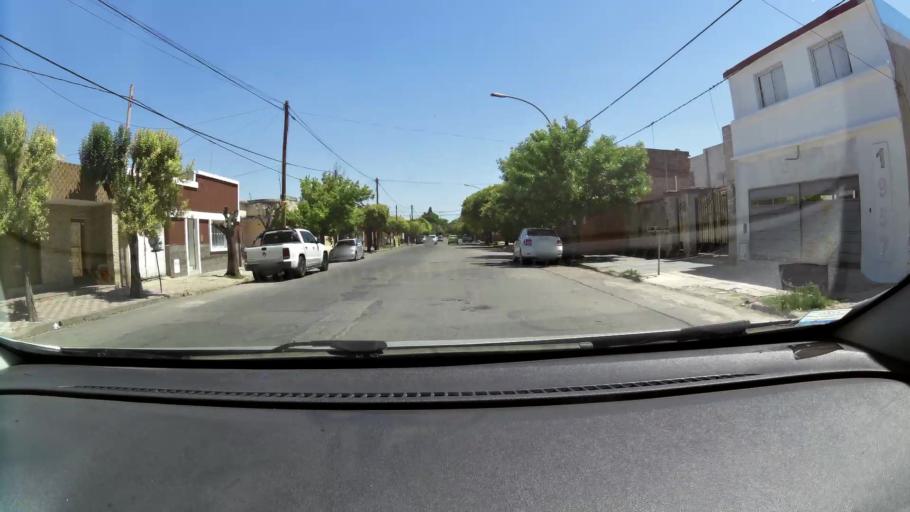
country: AR
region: Cordoba
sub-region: Departamento de Capital
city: Cordoba
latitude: -31.3876
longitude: -64.1501
